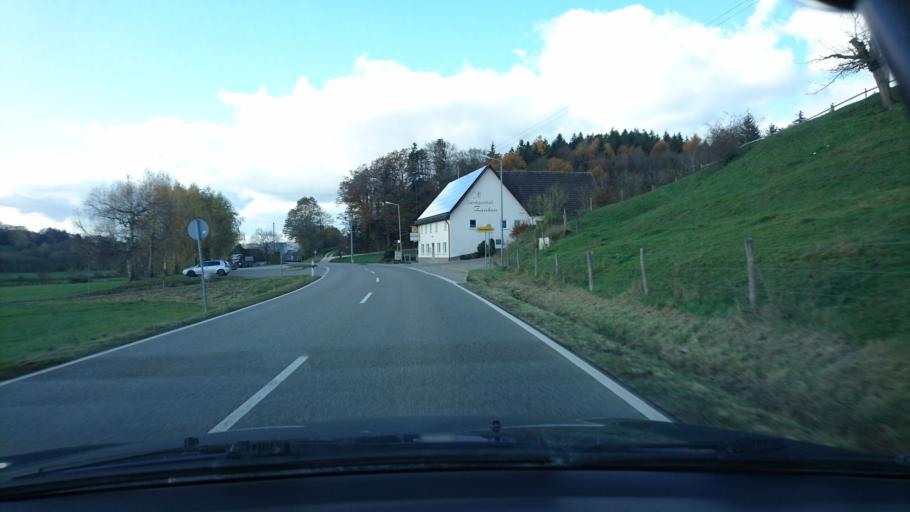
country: DE
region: Baden-Wuerttemberg
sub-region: Regierungsbezirk Stuttgart
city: Abtsgmund
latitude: 48.8957
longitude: 10.0424
